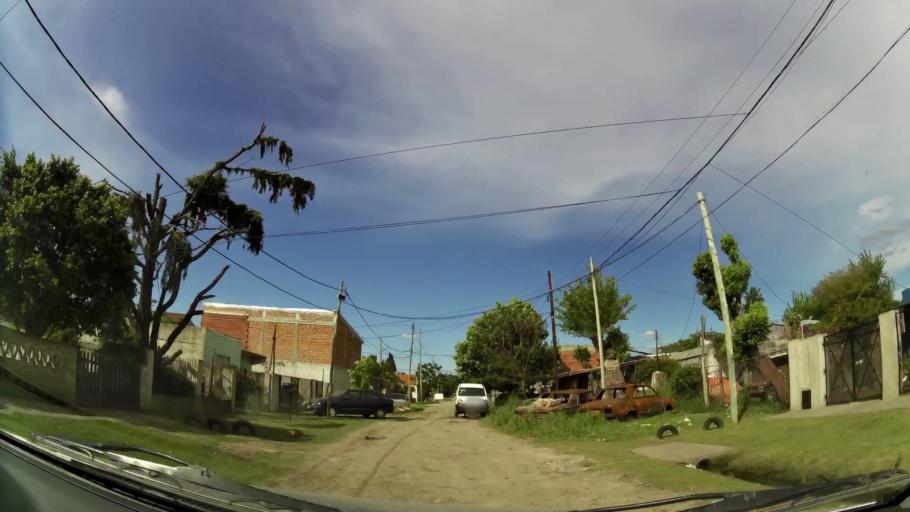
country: AR
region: Buenos Aires
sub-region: Partido de Almirante Brown
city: Adrogue
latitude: -34.8110
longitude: -58.3536
